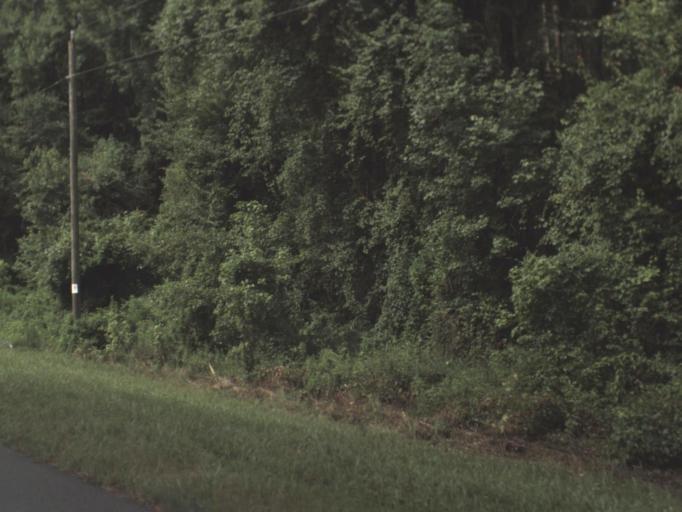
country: US
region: Florida
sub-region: Columbia County
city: Five Points
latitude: 30.4653
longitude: -82.6537
